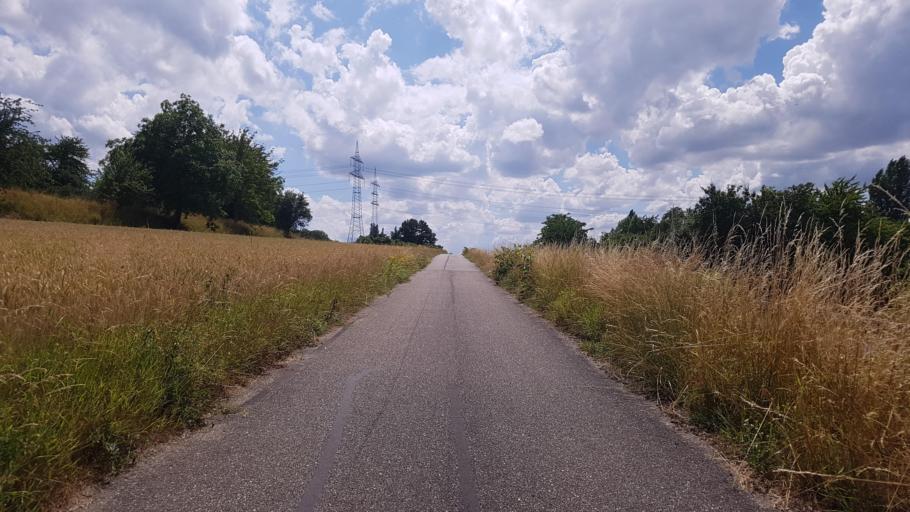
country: DE
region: Baden-Wuerttemberg
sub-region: Karlsruhe Region
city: Ubstadt-Weiher
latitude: 49.1544
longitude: 8.6249
